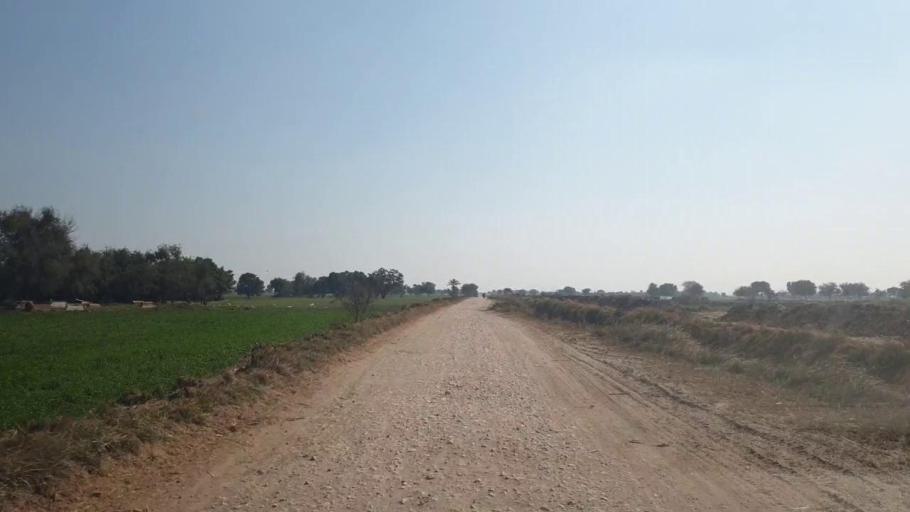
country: PK
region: Sindh
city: Shahdadpur
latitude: 25.9647
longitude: 68.6195
